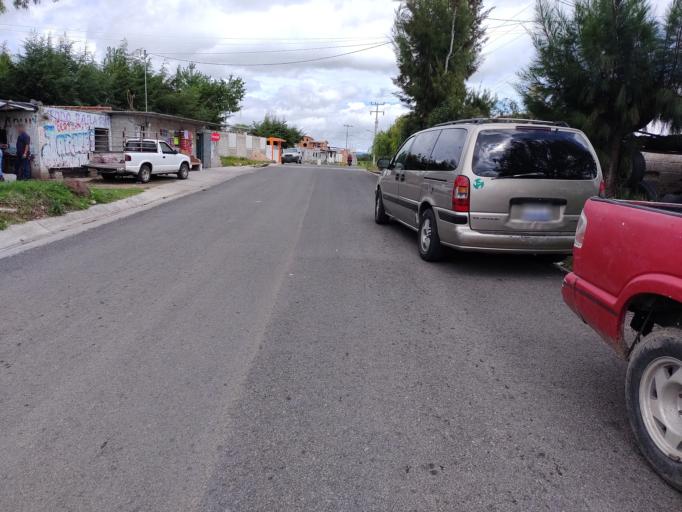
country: MX
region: Mexico
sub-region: Aculco
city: Gunyo Poniente (San Jose Gunyo)
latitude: 20.1156
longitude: -99.8739
